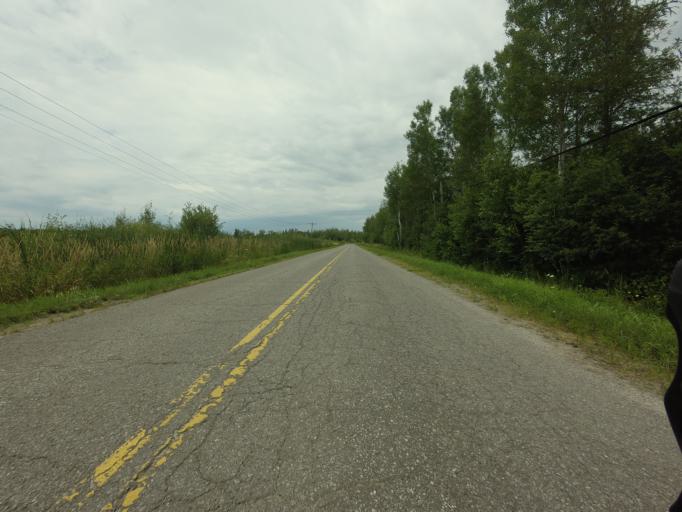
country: CA
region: Ontario
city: Prescott
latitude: 45.0240
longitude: -75.6222
